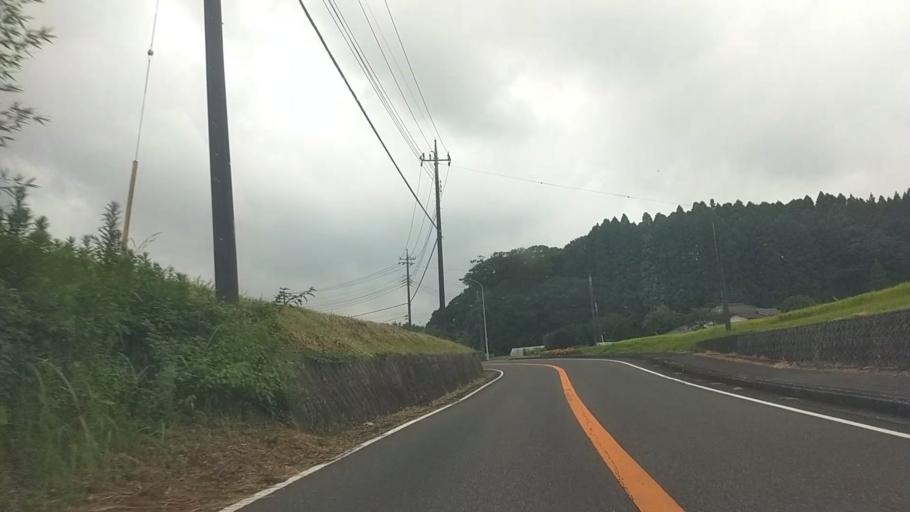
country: JP
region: Chiba
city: Kawaguchi
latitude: 35.2448
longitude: 140.0783
